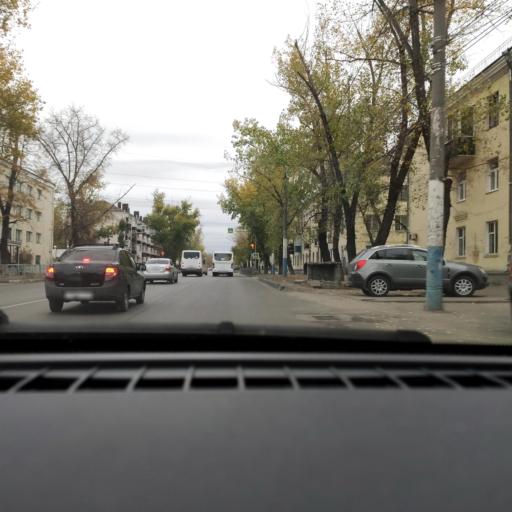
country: RU
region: Voronezj
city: Somovo
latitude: 51.7187
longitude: 39.2737
